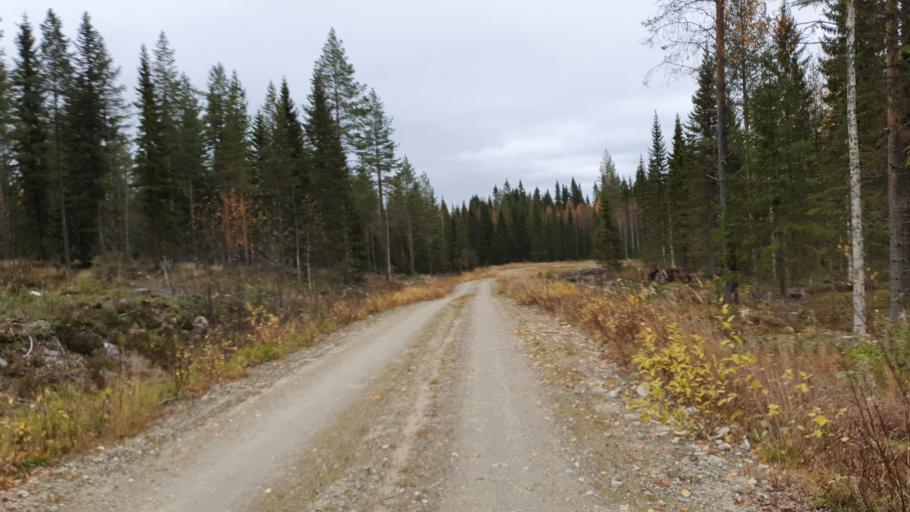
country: FI
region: Kainuu
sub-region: Kehys-Kainuu
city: Kuhmo
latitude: 64.4448
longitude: 29.6512
